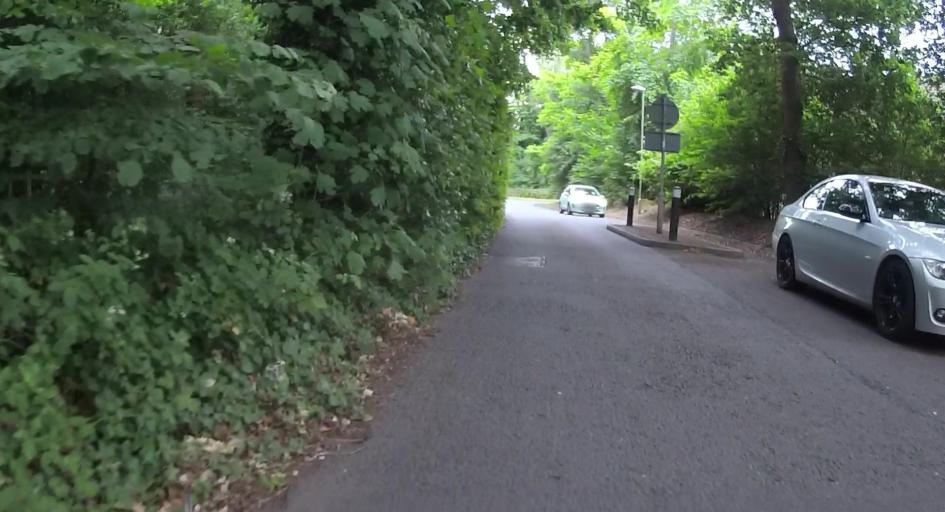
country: GB
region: England
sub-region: Hampshire
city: Fleet
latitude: 51.2537
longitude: -0.8264
